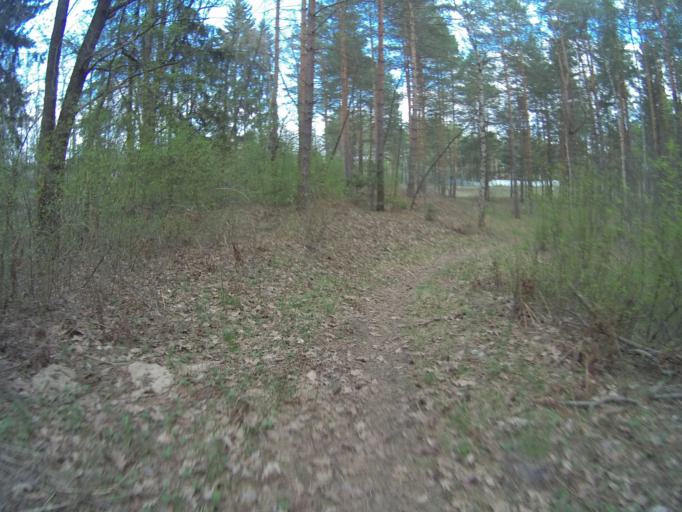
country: RU
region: Vladimir
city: Raduzhnyy
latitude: 56.0346
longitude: 40.3814
